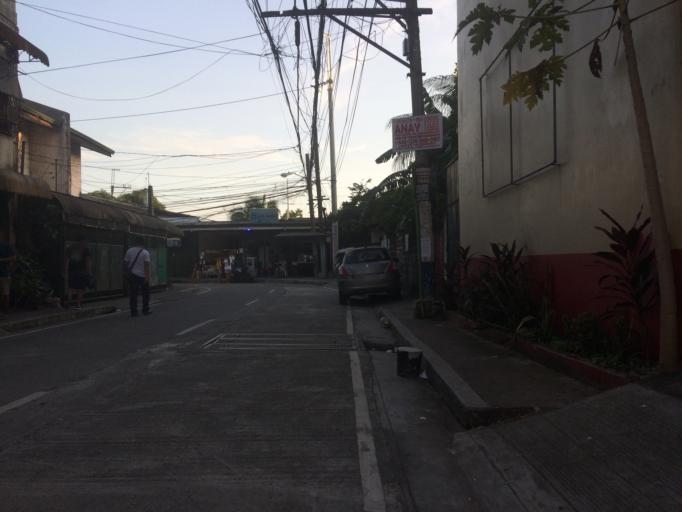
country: PH
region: Calabarzon
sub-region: Province of Rizal
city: Cainta
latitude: 14.5904
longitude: 121.1040
